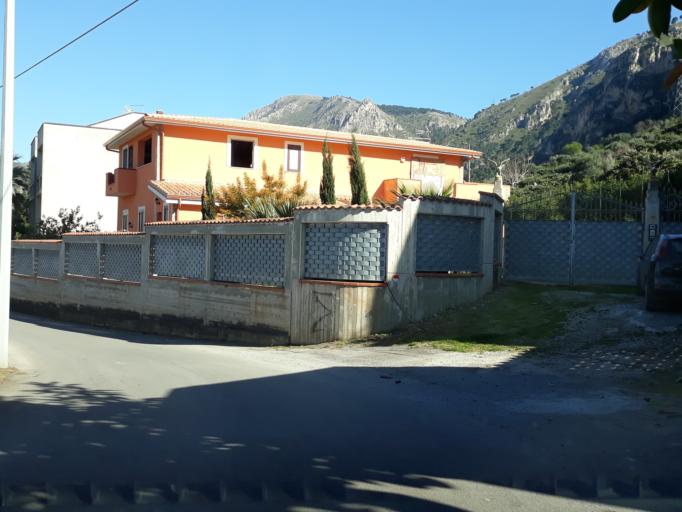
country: IT
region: Sicily
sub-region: Palermo
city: Villa Ciambra
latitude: 38.0756
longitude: 13.3499
